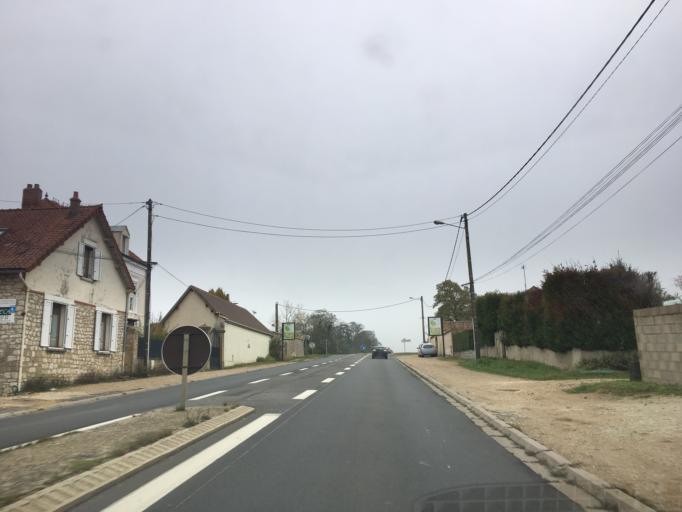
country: FR
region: Ile-de-France
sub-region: Departement de Seine-et-Marne
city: Cannes-Ecluse
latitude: 48.3600
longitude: 2.9725
